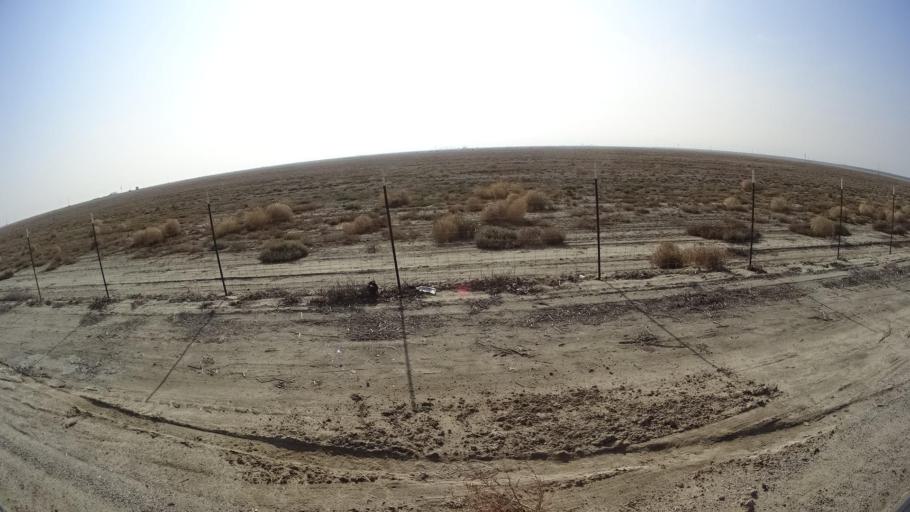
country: US
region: California
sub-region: Kern County
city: Buttonwillow
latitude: 35.3548
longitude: -119.3634
